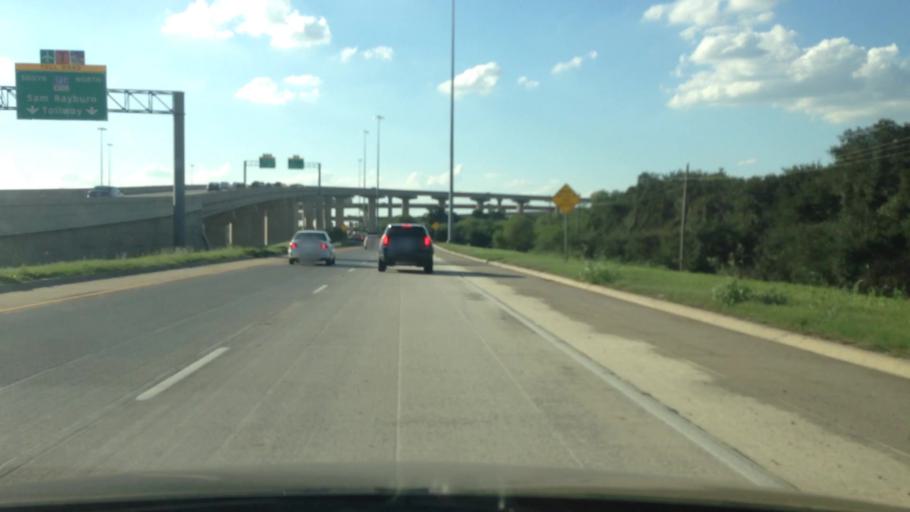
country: US
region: Texas
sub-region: Denton County
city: Lewisville
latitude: 32.9967
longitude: -96.9527
